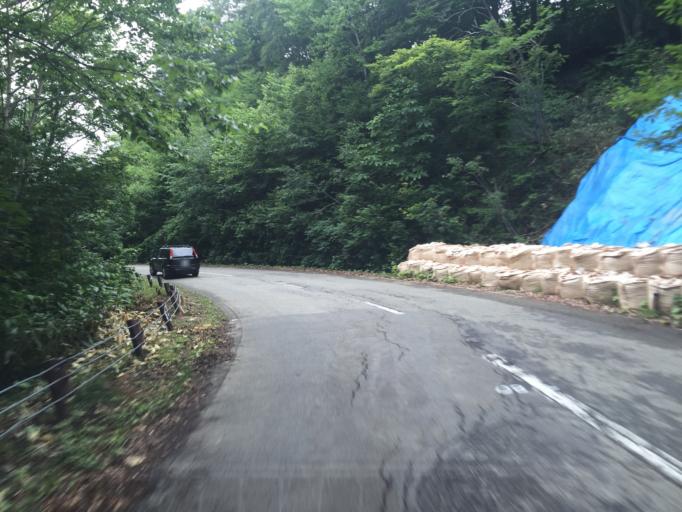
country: JP
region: Yamagata
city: Yonezawa
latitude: 37.7457
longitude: 140.0776
